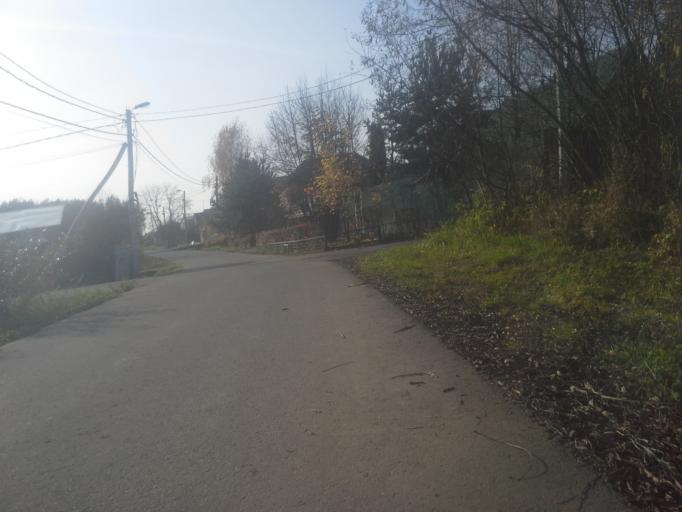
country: RU
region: Moskovskaya
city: Kokoshkino
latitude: 55.6114
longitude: 37.1603
